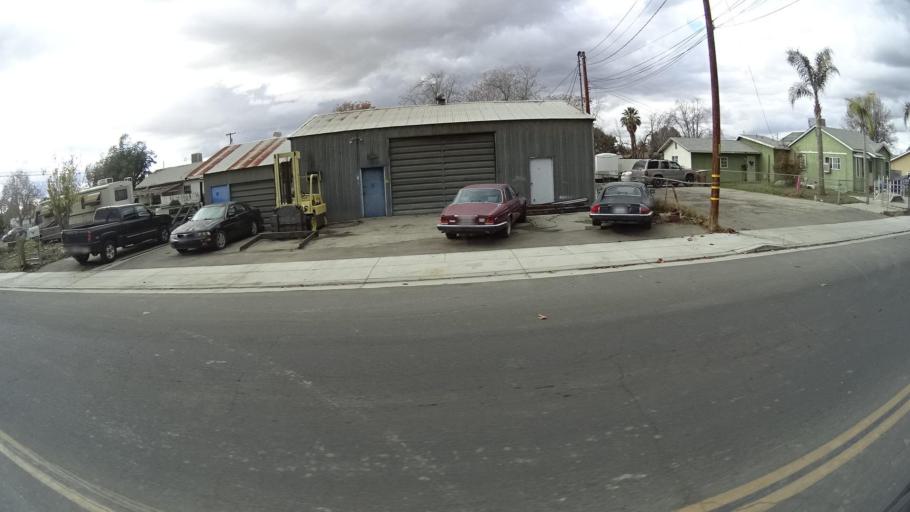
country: US
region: California
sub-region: Kern County
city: Greenfield
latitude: 35.3090
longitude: -118.9943
